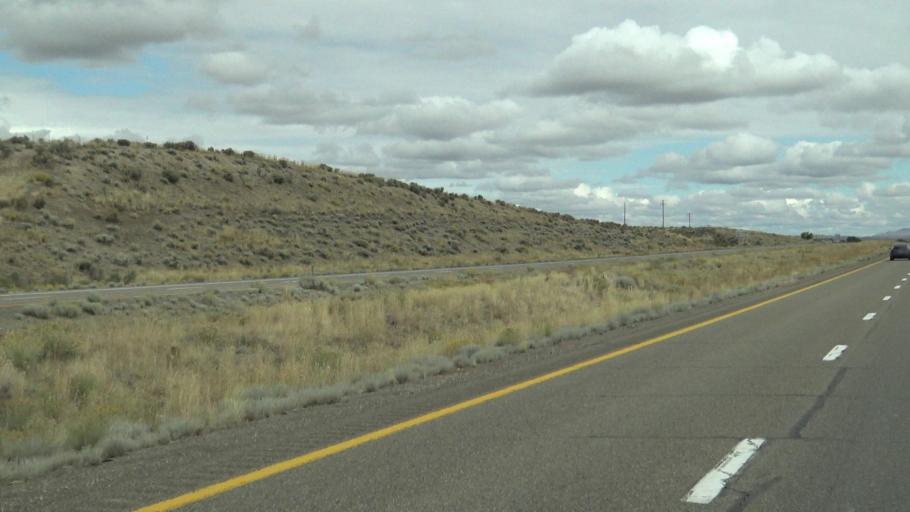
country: US
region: Nevada
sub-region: Elko County
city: Elko
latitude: 40.8732
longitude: -115.7246
